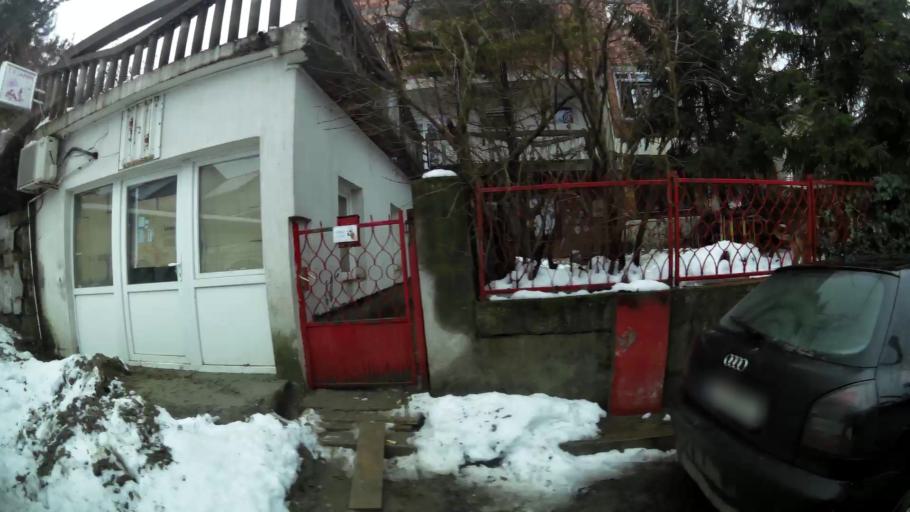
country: RS
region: Central Serbia
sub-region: Belgrade
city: Zvezdara
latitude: 44.7873
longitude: 20.5223
